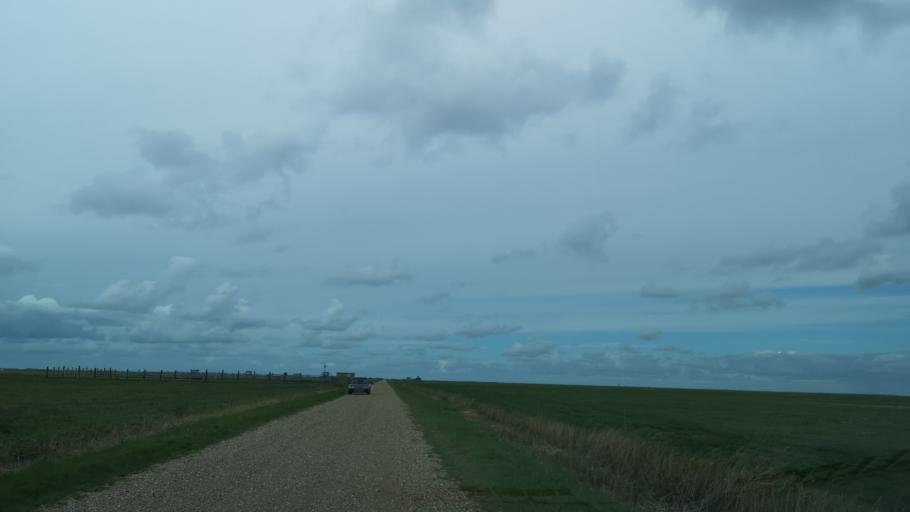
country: DK
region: Central Jutland
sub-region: Ringkobing-Skjern Kommune
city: Hvide Sande
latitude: 55.8758
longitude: 8.2260
